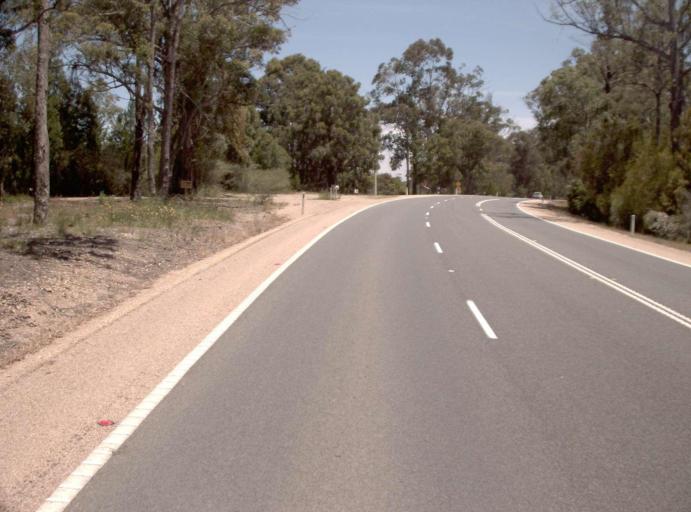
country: AU
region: Victoria
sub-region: East Gippsland
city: Bairnsdale
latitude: -37.7349
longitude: 147.7756
